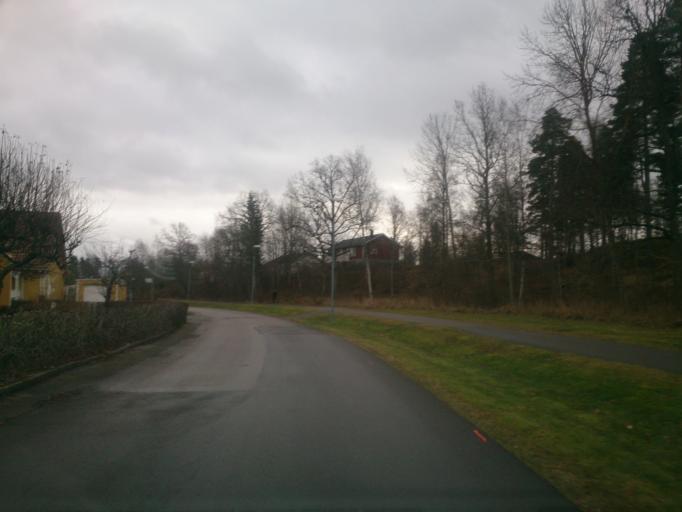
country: SE
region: OEstergoetland
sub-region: Atvidabergs Kommun
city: Atvidaberg
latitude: 58.2006
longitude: 15.9802
